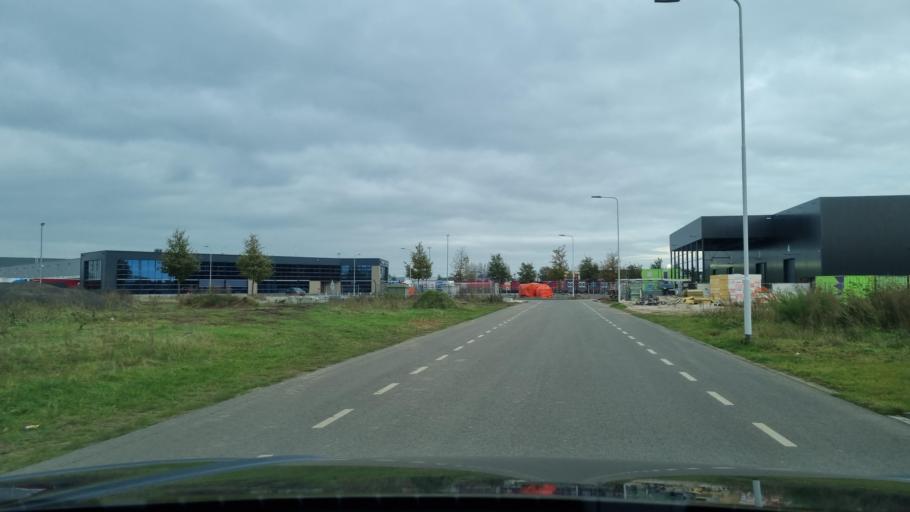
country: NL
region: Gelderland
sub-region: Gemeente Doetinchem
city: Doetinchem
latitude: 51.9460
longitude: 6.2245
